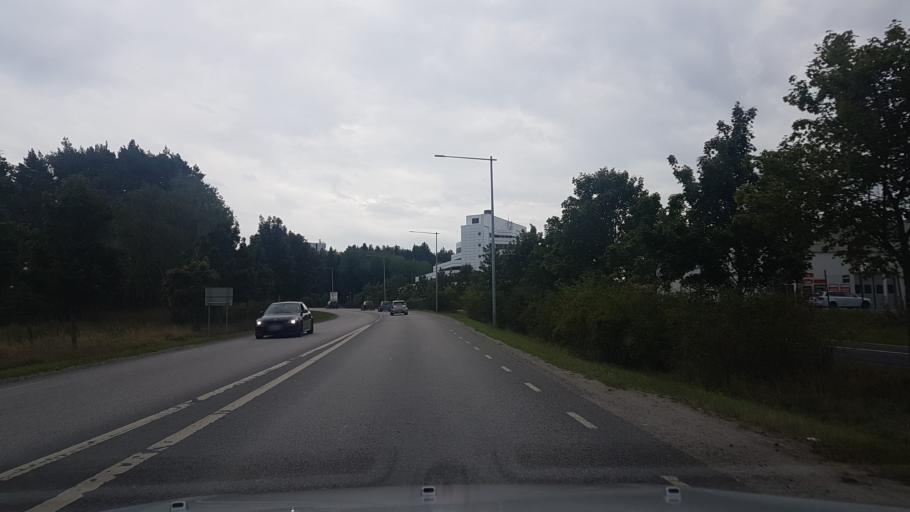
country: SE
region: Stockholm
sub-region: Jarfalla Kommun
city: Jakobsberg
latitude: 59.4135
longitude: 17.8286
